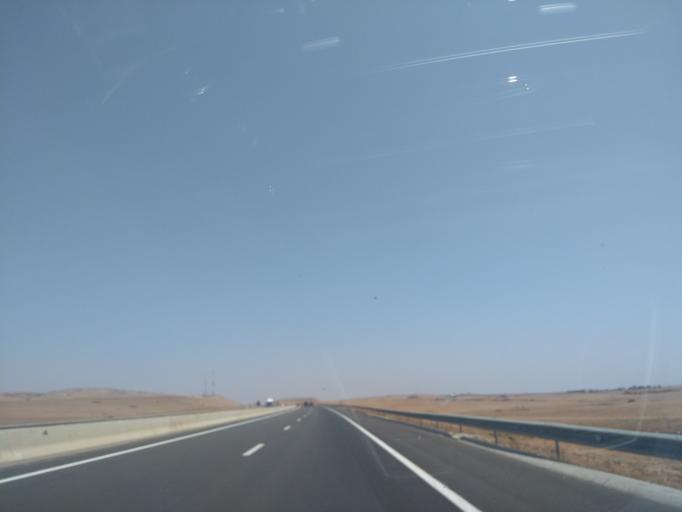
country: MA
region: Marrakech-Tensift-Al Haouz
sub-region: Kelaa-Des-Sraghna
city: Sidi Abdallah
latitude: 32.2998
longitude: -7.9596
